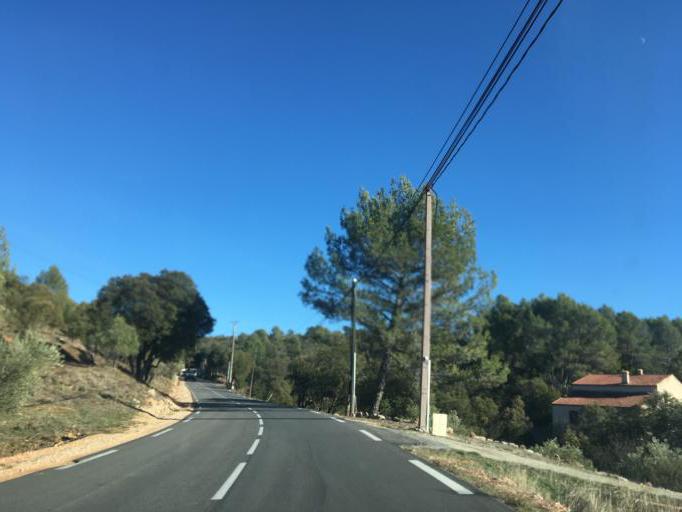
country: FR
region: Provence-Alpes-Cote d'Azur
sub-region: Departement du Var
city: Barjols
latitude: 43.5948
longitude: 6.0289
